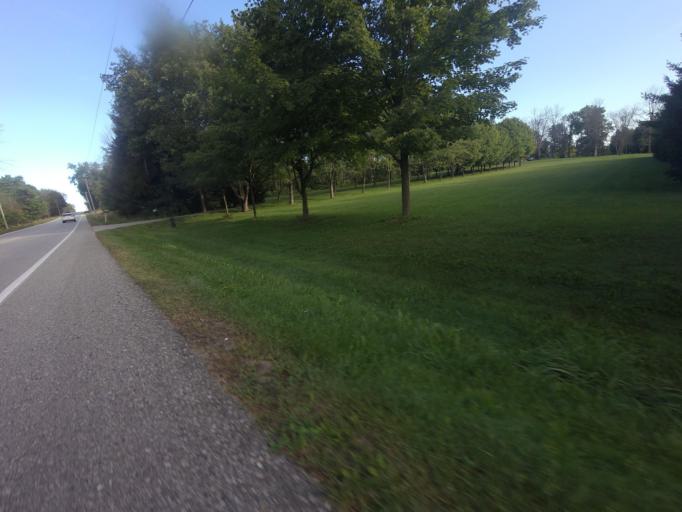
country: CA
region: Ontario
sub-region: Wellington County
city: Guelph
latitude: 43.5851
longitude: -80.3427
